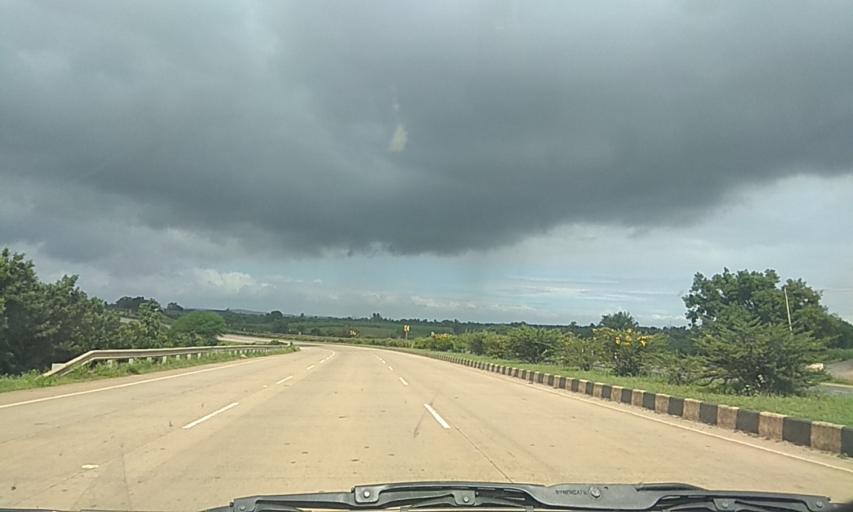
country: IN
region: Karnataka
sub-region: Dharwad
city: Alnavar
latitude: 15.5486
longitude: 74.8618
